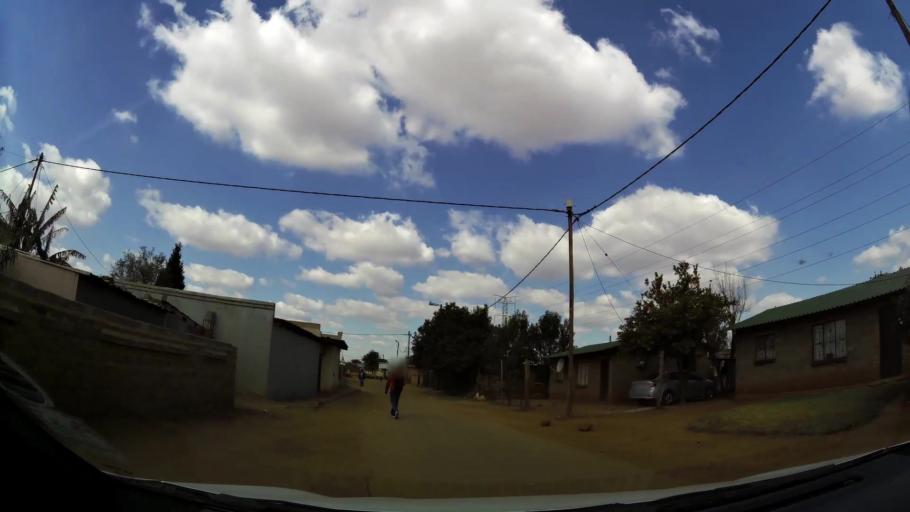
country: ZA
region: Gauteng
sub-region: City of Tshwane Metropolitan Municipality
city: Cullinan
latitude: -25.7058
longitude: 28.3957
